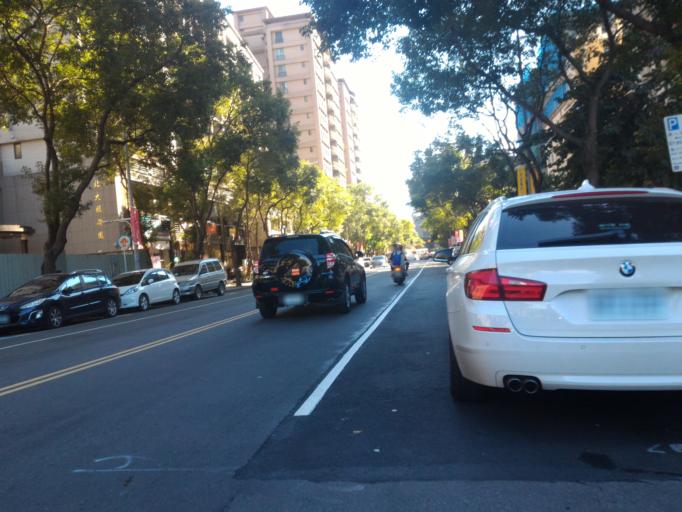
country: TW
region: Taiwan
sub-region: Taoyuan
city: Taoyuan
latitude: 24.9442
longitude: 121.3743
